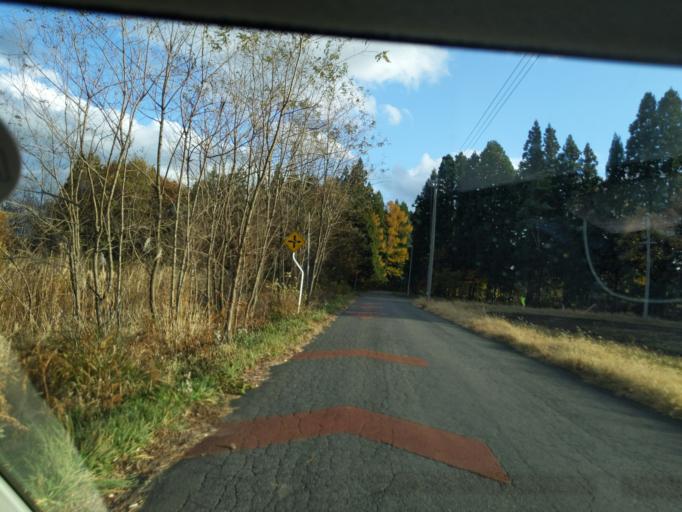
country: JP
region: Iwate
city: Mizusawa
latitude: 39.1169
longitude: 140.9989
